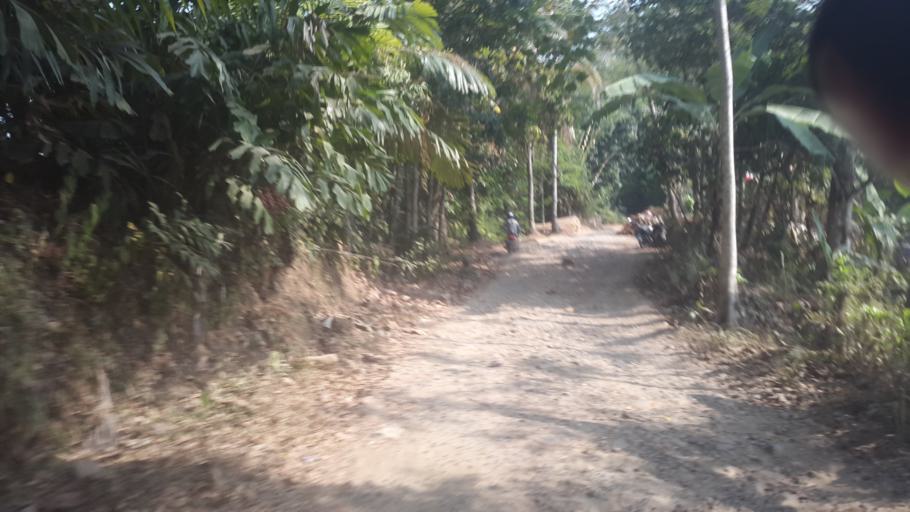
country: ID
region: West Java
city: Tugu
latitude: -6.9414
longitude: 106.4447
